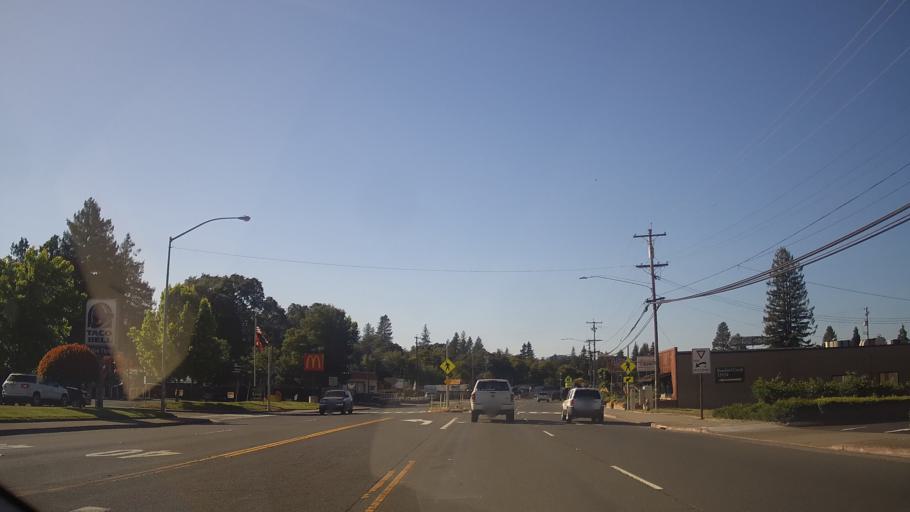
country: US
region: California
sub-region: Mendocino County
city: Willits
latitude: 39.3942
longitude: -123.3487
